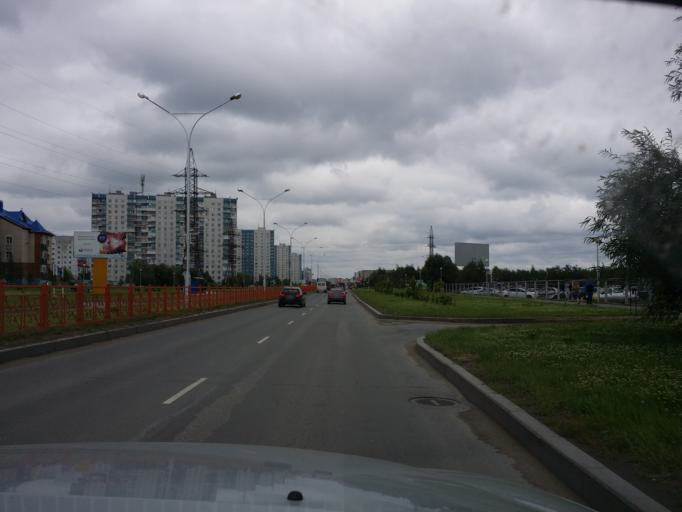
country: RU
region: Khanty-Mansiyskiy Avtonomnyy Okrug
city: Nizhnevartovsk
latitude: 60.9559
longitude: 76.5726
